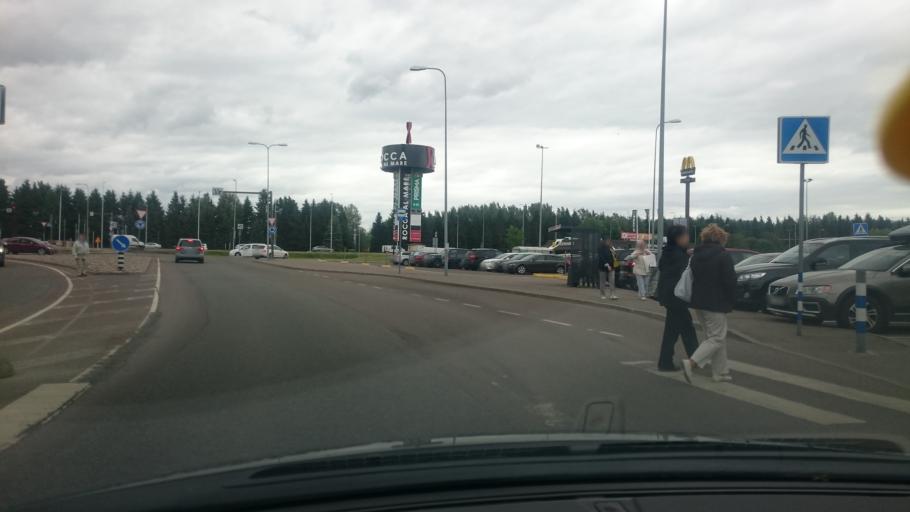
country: EE
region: Harju
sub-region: Saue vald
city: Laagri
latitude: 59.4270
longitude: 24.6550
